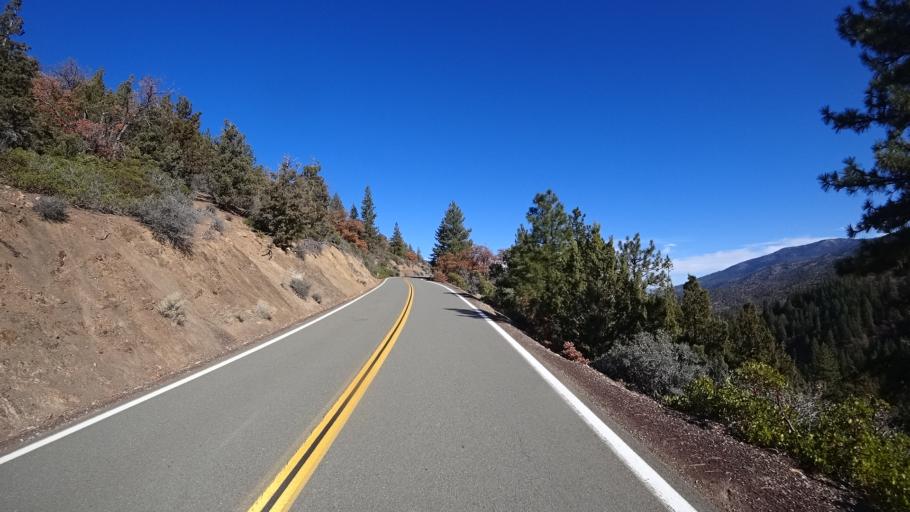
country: US
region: California
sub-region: Siskiyou County
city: Weed
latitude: 41.4507
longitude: -122.6427
